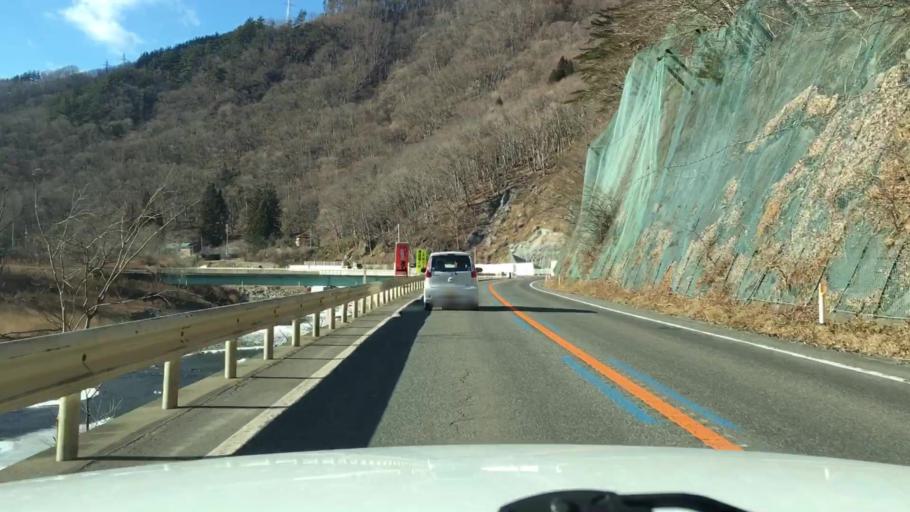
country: JP
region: Iwate
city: Miyako
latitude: 39.5998
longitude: 141.7353
